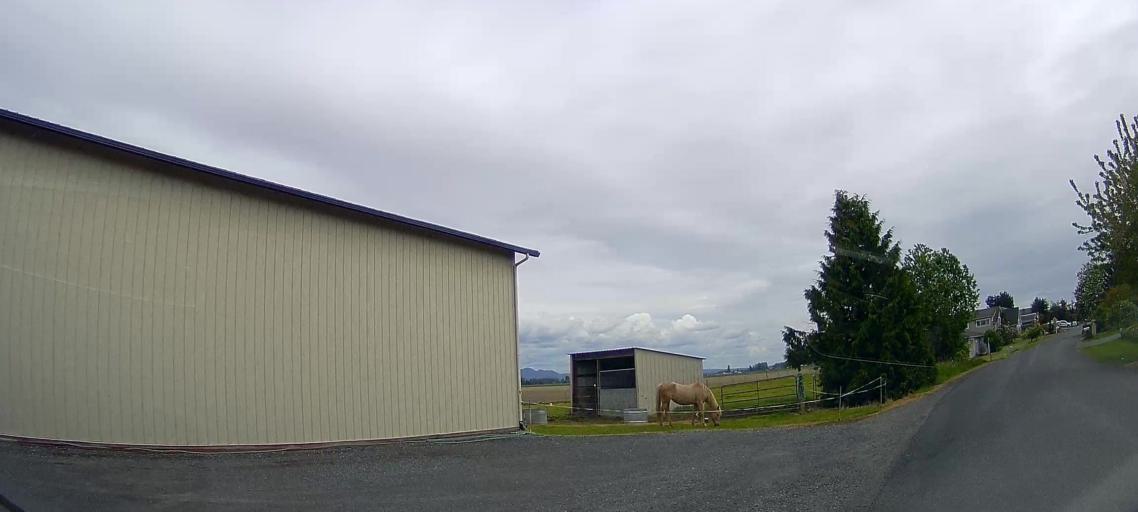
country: US
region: Washington
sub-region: Skagit County
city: Anacortes
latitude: 48.4337
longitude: -122.4978
